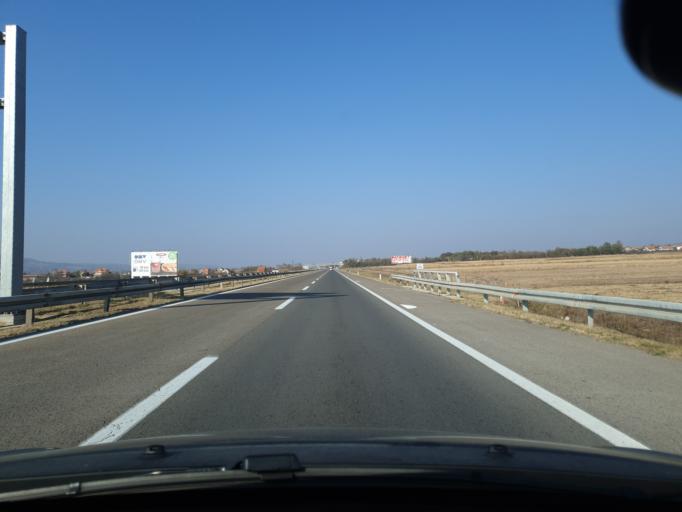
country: RS
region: Central Serbia
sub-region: Nisavski Okrug
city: Nis
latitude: 43.3701
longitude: 21.8176
